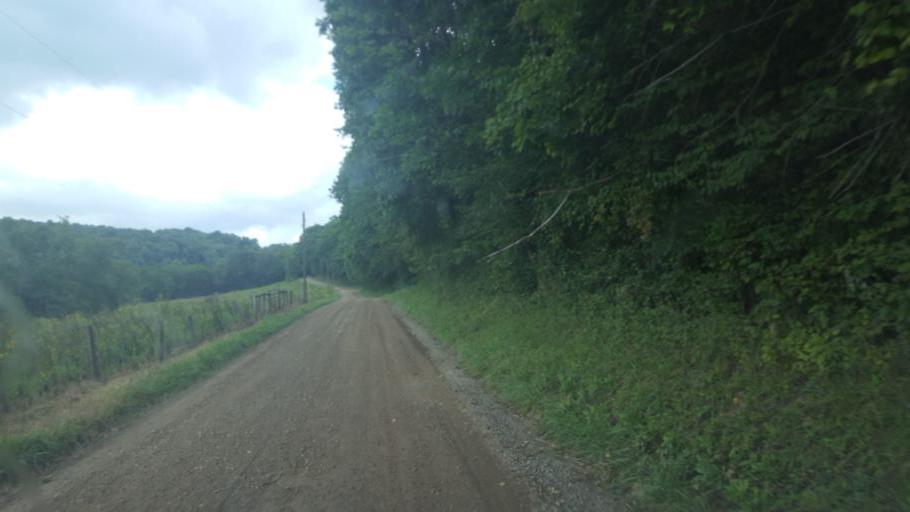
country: US
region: Ohio
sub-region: Knox County
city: Oak Hill
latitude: 40.3877
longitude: -82.2331
